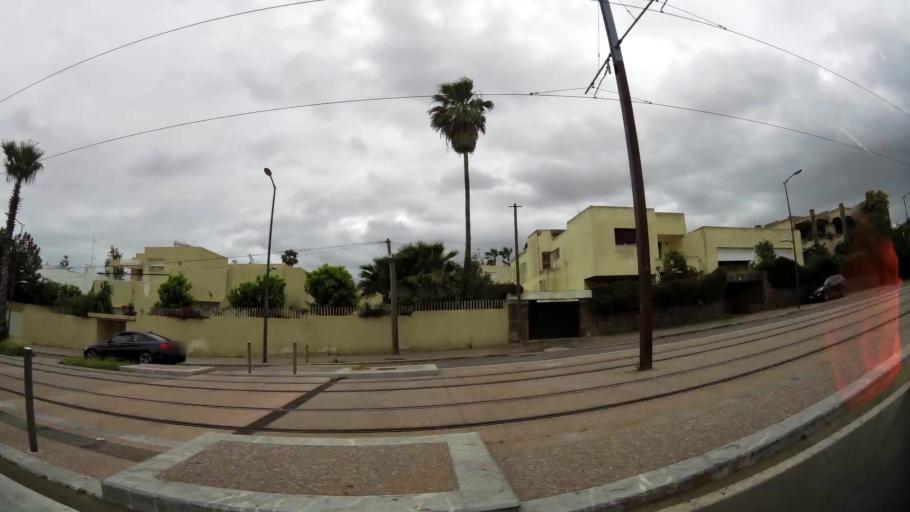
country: MA
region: Grand Casablanca
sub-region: Casablanca
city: Casablanca
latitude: 33.5484
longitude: -7.6320
